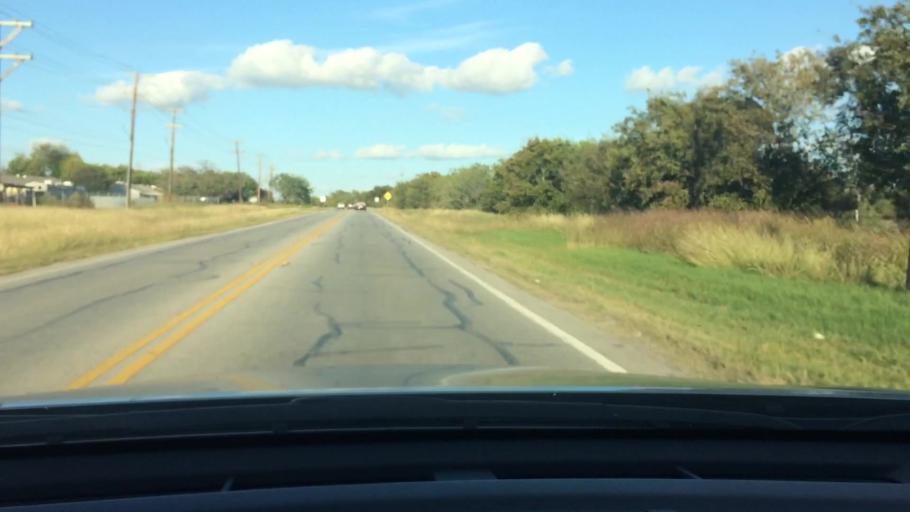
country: US
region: Texas
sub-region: Bexar County
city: Converse
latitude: 29.4994
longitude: -98.3463
